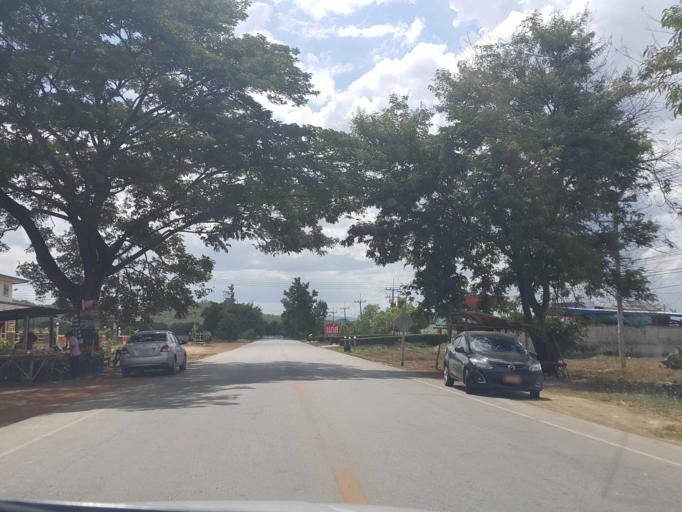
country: TH
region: Sukhothai
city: Thung Saliam
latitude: 17.3417
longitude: 99.6024
